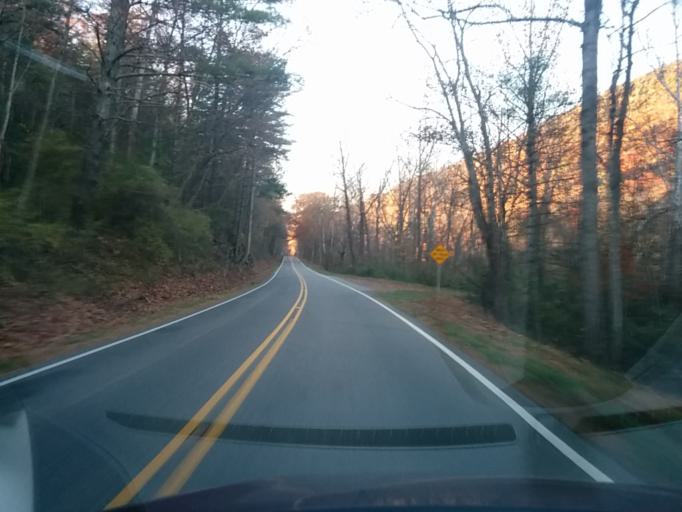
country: US
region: Virginia
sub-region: Rockbridge County
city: East Lexington
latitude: 37.9644
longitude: -79.4850
